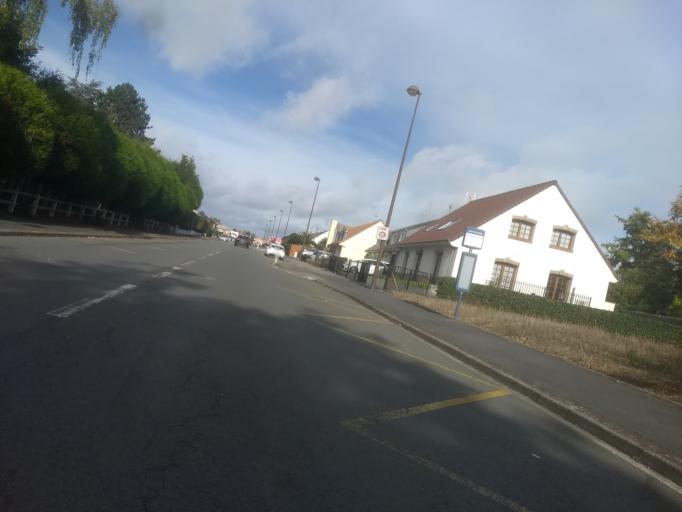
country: FR
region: Nord-Pas-de-Calais
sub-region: Departement du Pas-de-Calais
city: Achicourt
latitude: 50.2874
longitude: 2.7444
